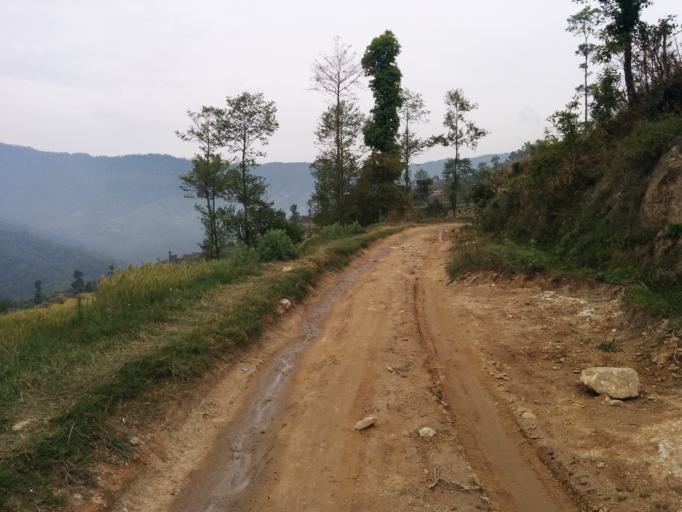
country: NP
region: Central Region
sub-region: Bagmati Zone
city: Bhaktapur
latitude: 27.7750
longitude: 85.4295
